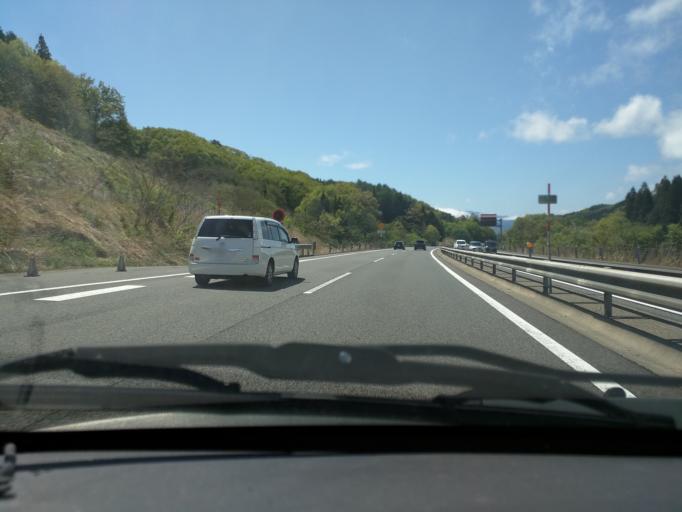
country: JP
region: Nagano
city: Nakano
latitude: 36.7934
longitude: 138.3220
